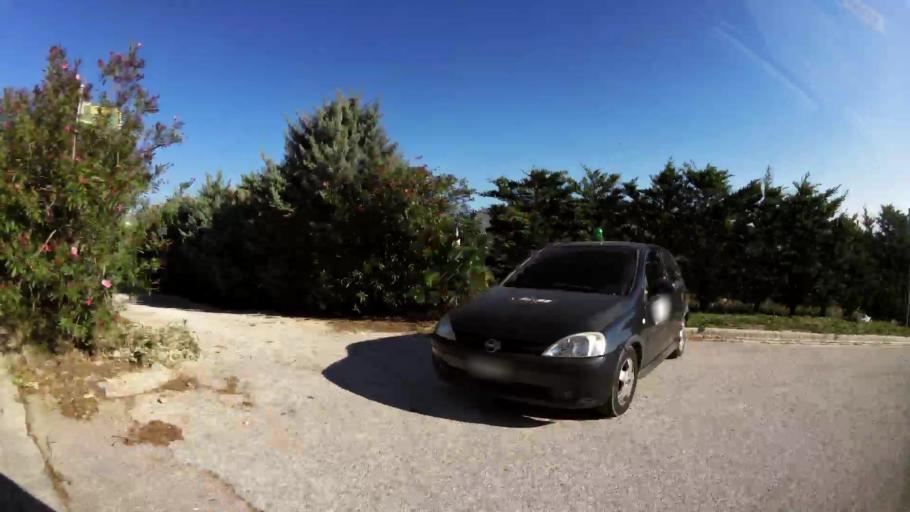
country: GR
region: Attica
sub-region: Nomarchia Anatolikis Attikis
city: Dhrafi
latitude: 38.0245
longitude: 23.9026
